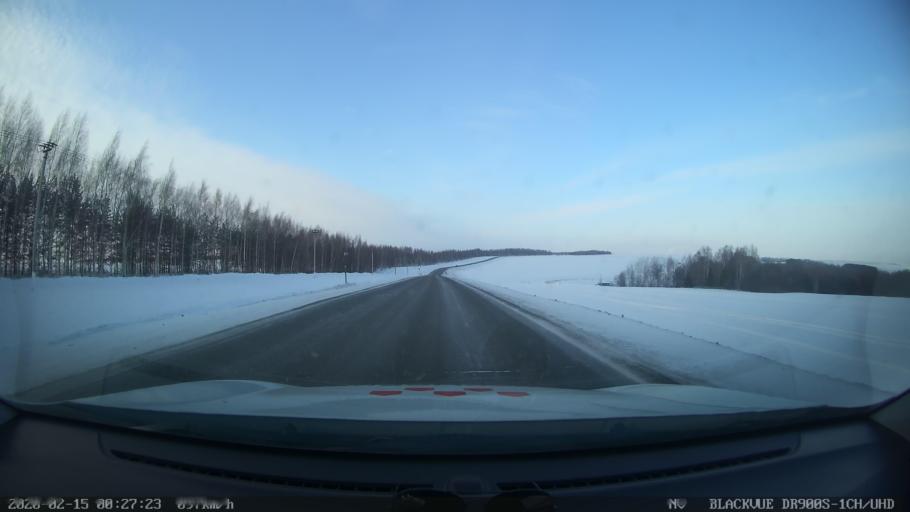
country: RU
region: Tatarstan
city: Verkhniy Uslon
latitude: 55.6274
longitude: 48.8749
